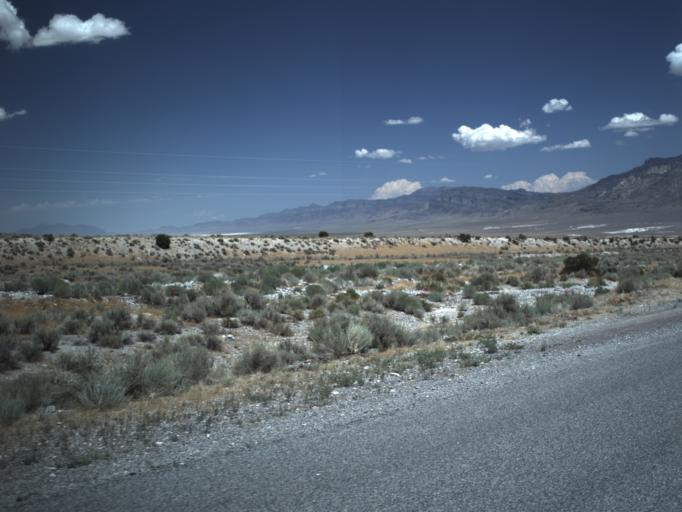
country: US
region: Utah
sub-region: Beaver County
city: Milford
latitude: 39.0871
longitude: -113.5561
